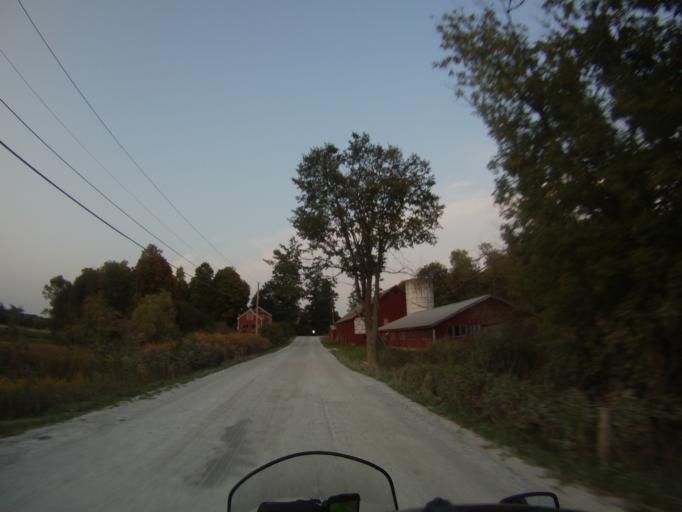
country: US
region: Vermont
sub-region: Rutland County
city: Brandon
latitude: 43.7886
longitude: -73.1132
